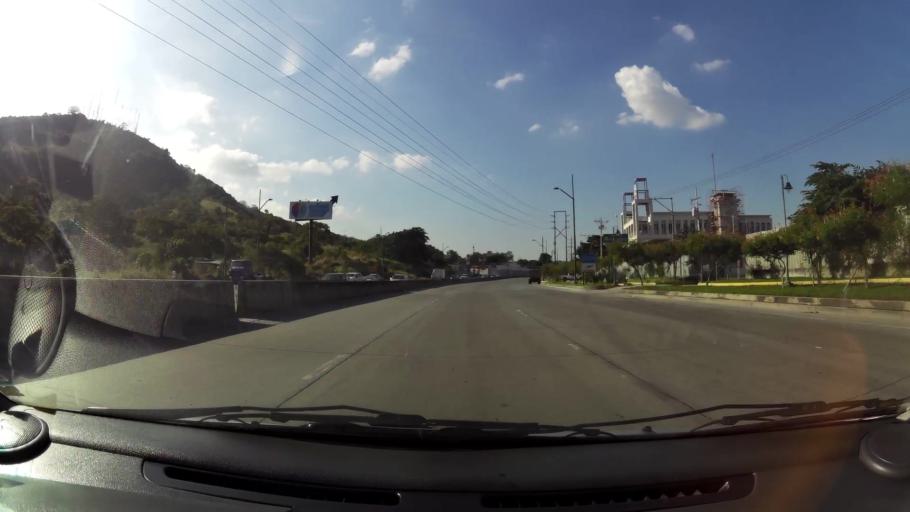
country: EC
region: Guayas
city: Guayaquil
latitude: -2.1810
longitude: -79.9455
